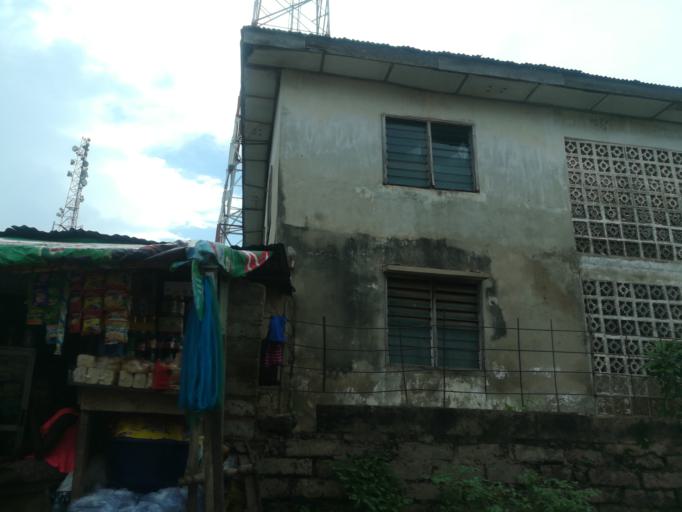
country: NG
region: Oyo
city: Ibadan
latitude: 7.4155
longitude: 3.8983
